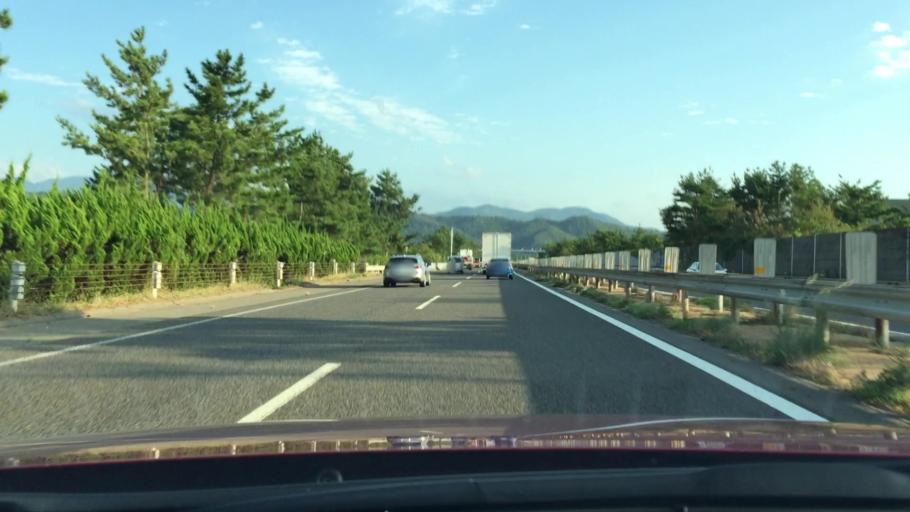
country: JP
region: Shiga Prefecture
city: Nagahama
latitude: 35.3693
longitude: 136.3048
